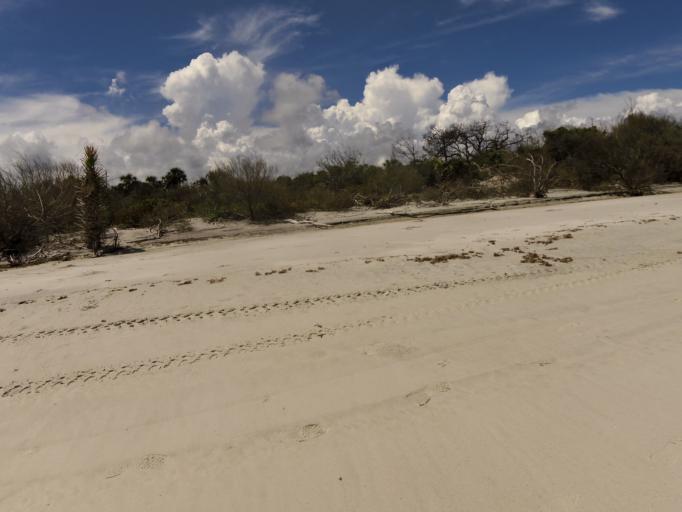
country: US
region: Florida
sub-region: Duval County
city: Atlantic Beach
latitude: 30.4713
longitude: -81.4127
